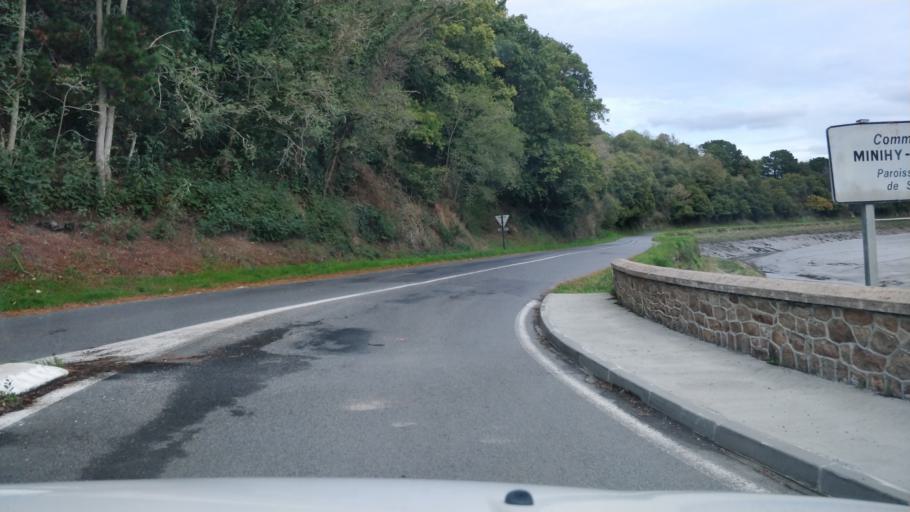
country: FR
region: Brittany
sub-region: Departement des Cotes-d'Armor
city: La Roche-Derrien
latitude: 48.7500
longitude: -3.2677
